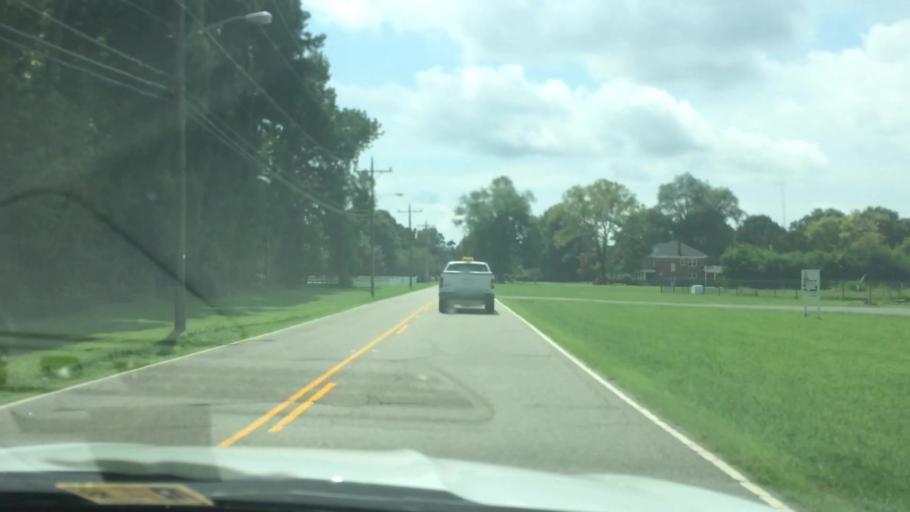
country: US
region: Virginia
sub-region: York County
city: Yorktown
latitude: 37.1979
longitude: -76.5718
